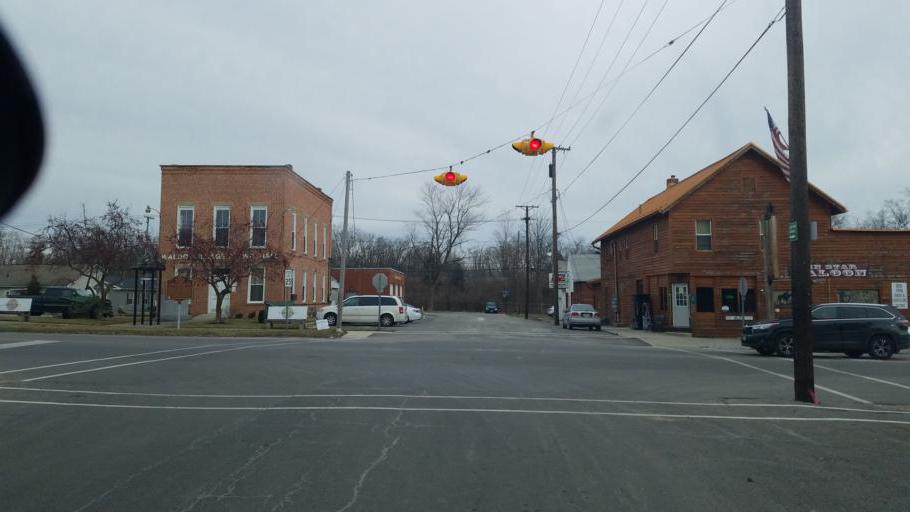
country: US
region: Ohio
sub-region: Marion County
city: Prospect
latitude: 40.4590
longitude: -83.0775
